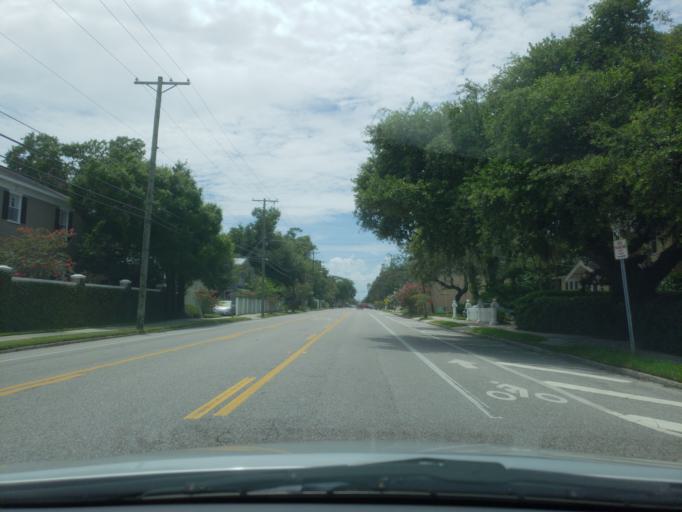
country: US
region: Florida
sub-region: Hillsborough County
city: Tampa
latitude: 27.9373
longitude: -82.4707
